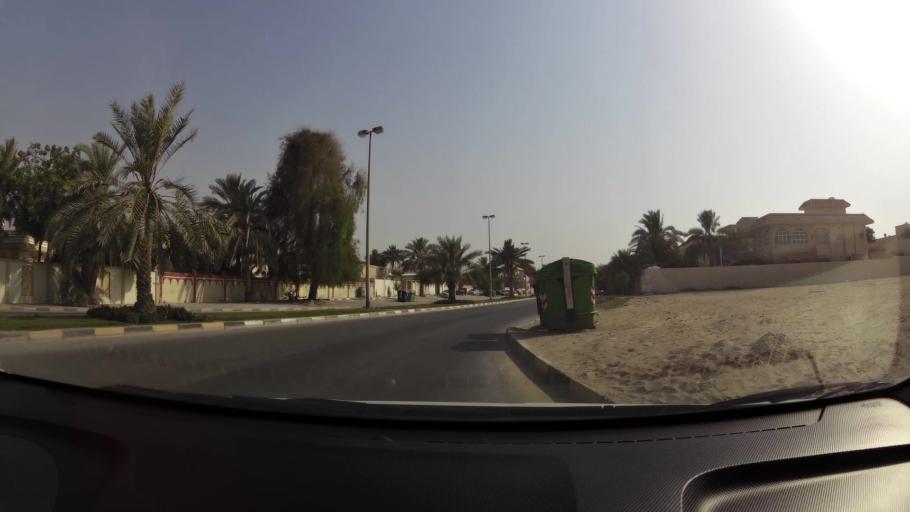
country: AE
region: Ajman
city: Ajman
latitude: 25.3858
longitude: 55.4334
